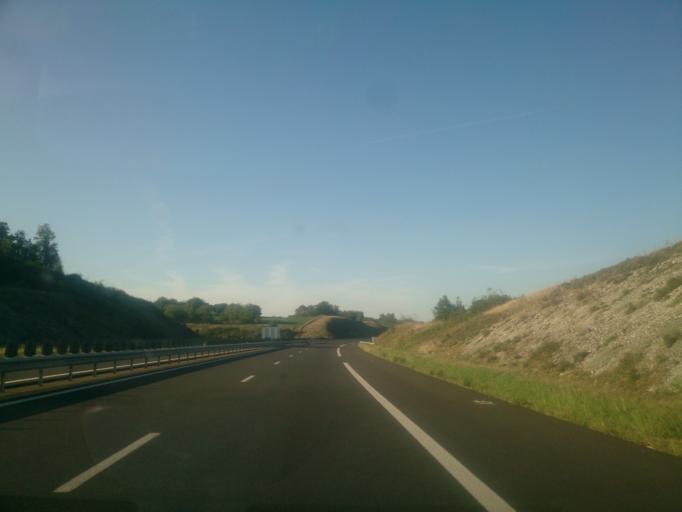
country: FR
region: Midi-Pyrenees
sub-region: Departement du Lot
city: Le Vigan
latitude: 44.6133
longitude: 1.5001
